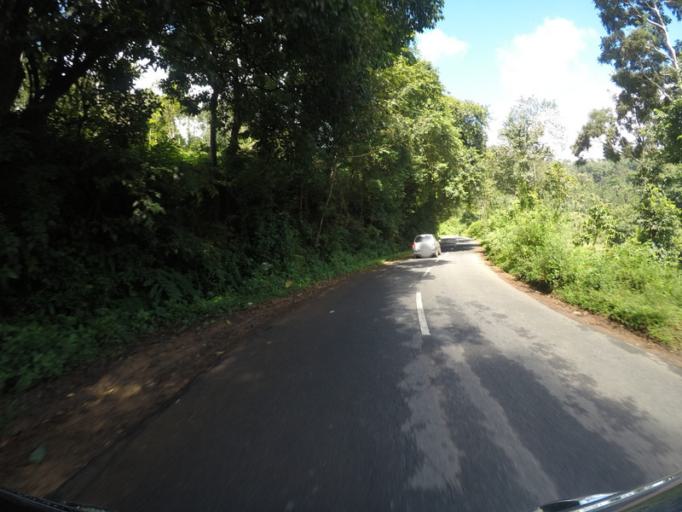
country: IN
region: Karnataka
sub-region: Kodagu
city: Suntikoppa
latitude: 12.4761
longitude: 75.7877
